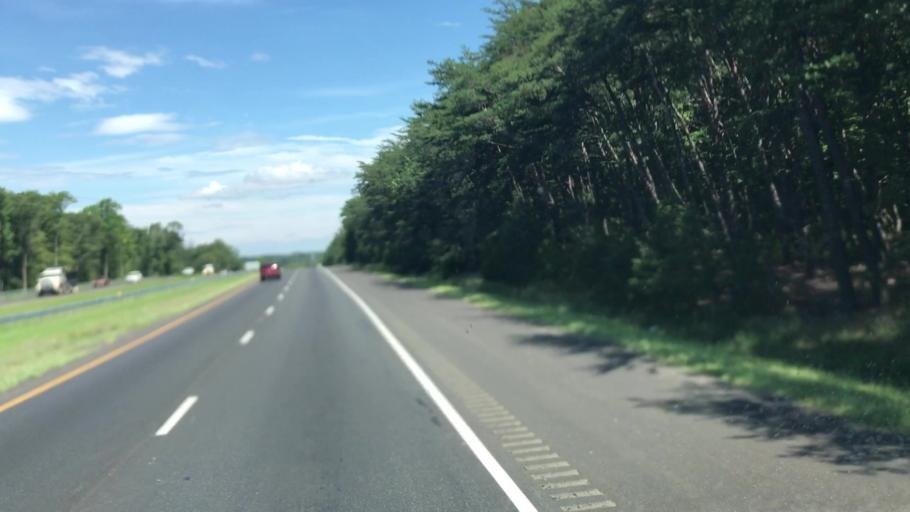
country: US
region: Maryland
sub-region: Prince George's County
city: Brandywine
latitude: 38.7171
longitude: -76.8783
